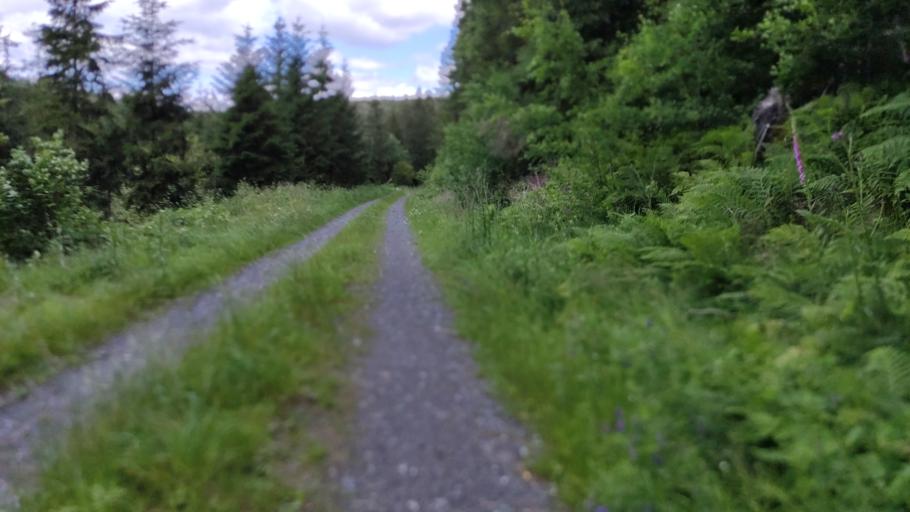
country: DE
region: Bavaria
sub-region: Upper Franconia
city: Tschirn
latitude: 50.4084
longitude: 11.4665
